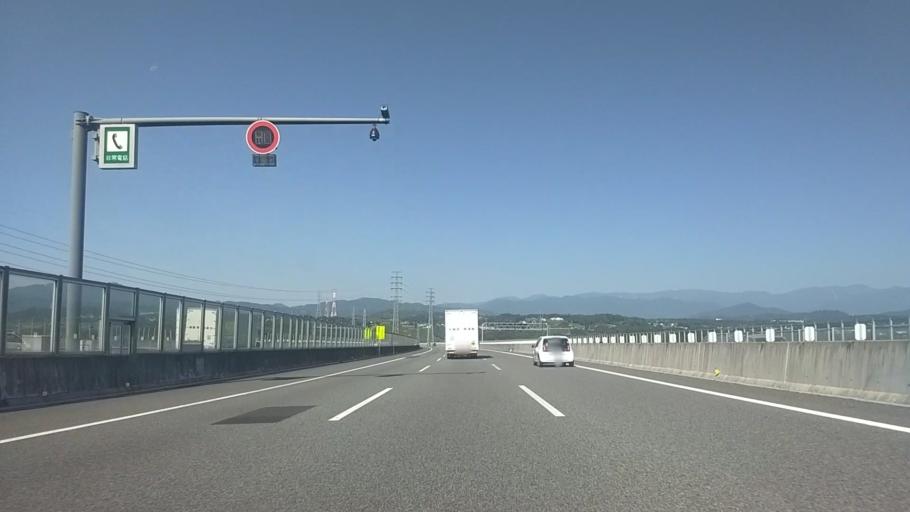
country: JP
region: Shizuoka
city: Fujinomiya
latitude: 35.1980
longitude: 138.6534
